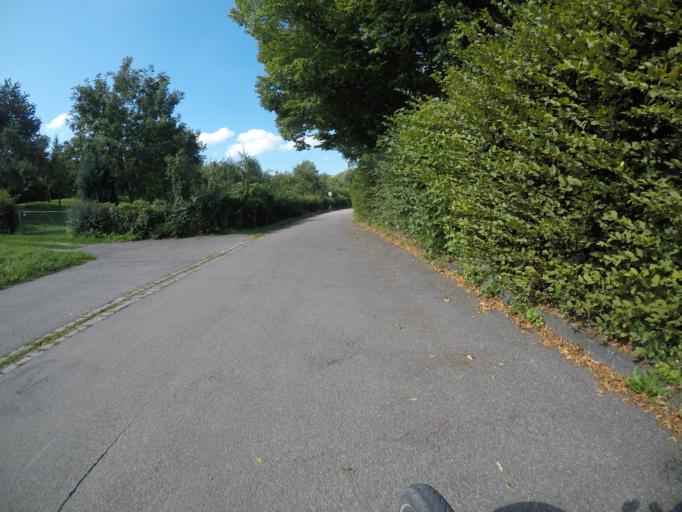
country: DE
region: Baden-Wuerttemberg
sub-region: Regierungsbezirk Stuttgart
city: Nurtingen
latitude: 48.6219
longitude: 9.3235
